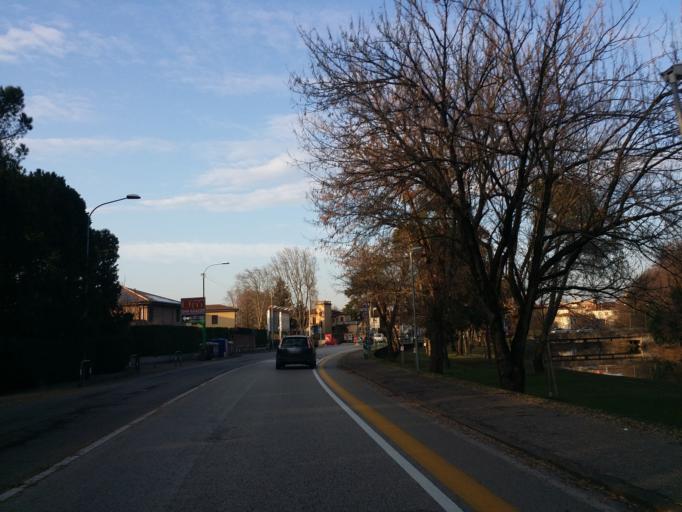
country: IT
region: Veneto
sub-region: Provincia di Padova
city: Padova
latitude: 45.3978
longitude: 11.8646
